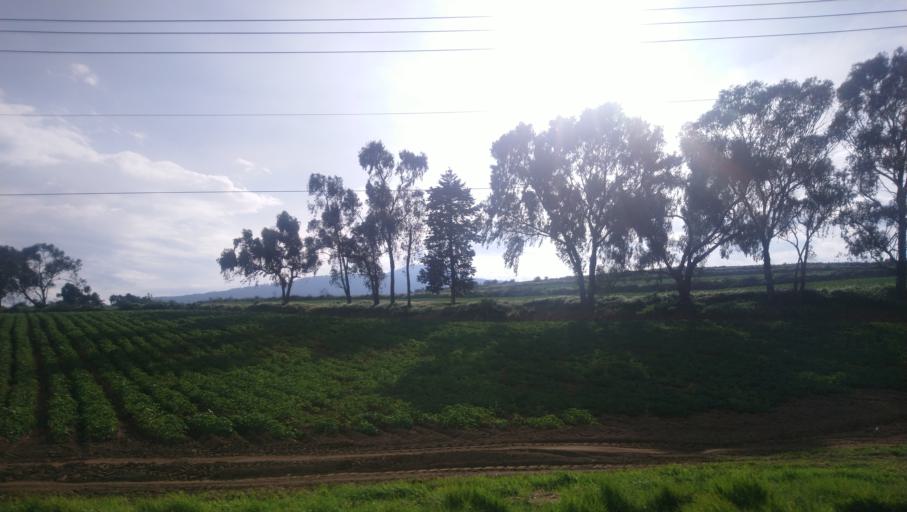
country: MX
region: Mexico
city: Juchitepec de Mariano Riva Palacio
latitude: 19.1203
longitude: -98.9370
